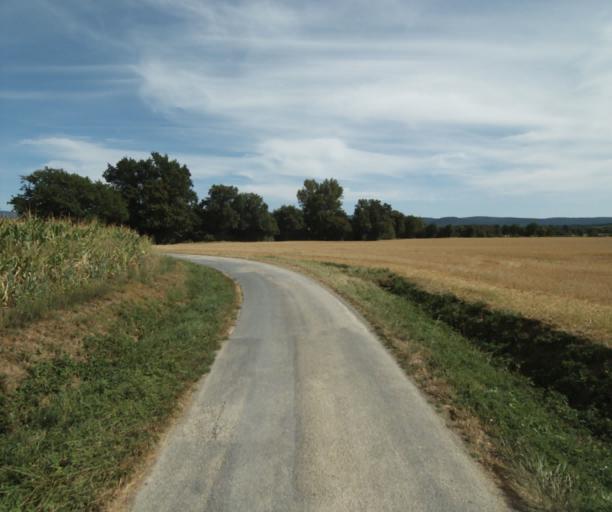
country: FR
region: Midi-Pyrenees
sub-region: Departement du Tarn
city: Soreze
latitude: 43.5125
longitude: 2.0689
